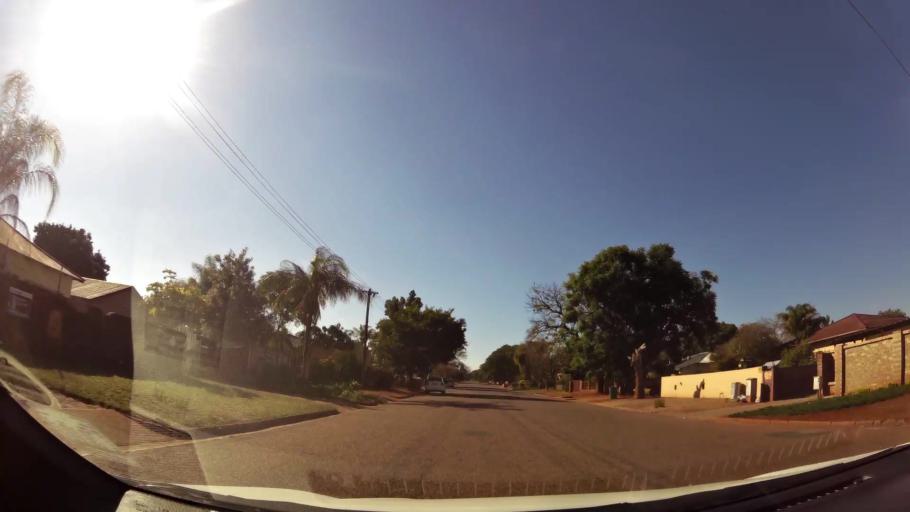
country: ZA
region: Limpopo
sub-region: Waterberg District Municipality
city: Mokopane
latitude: -24.1908
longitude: 29.0013
